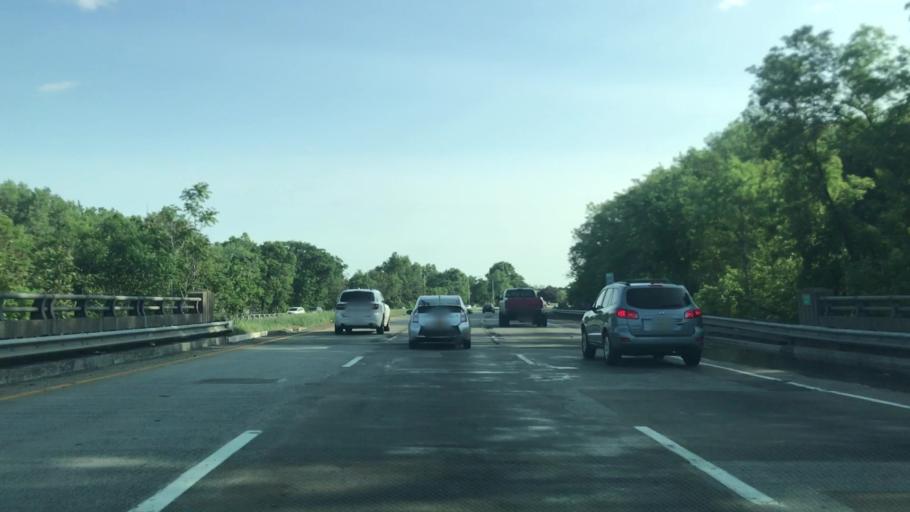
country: US
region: New Jersey
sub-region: Essex County
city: Fairfield
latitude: 40.8675
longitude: -74.3314
